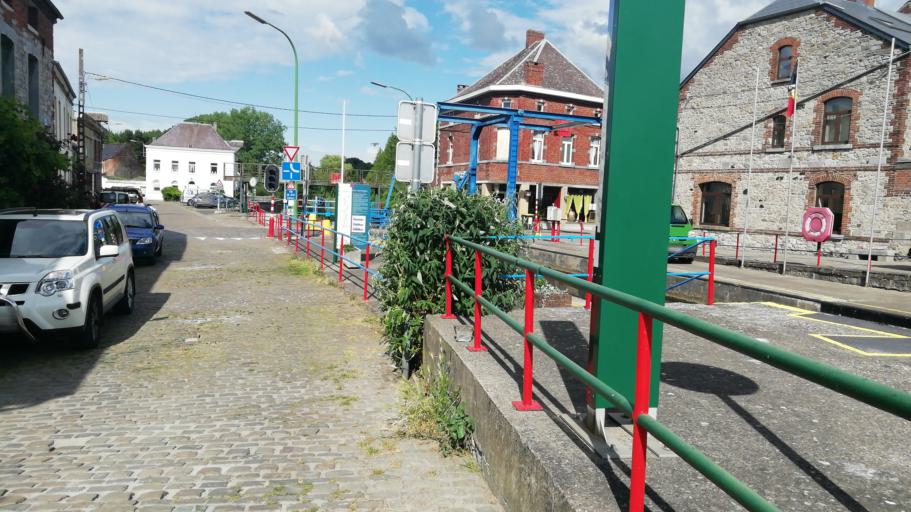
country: BE
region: Wallonia
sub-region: Province du Hainaut
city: Merbes-le-Chateau
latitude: 50.3142
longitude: 4.1938
